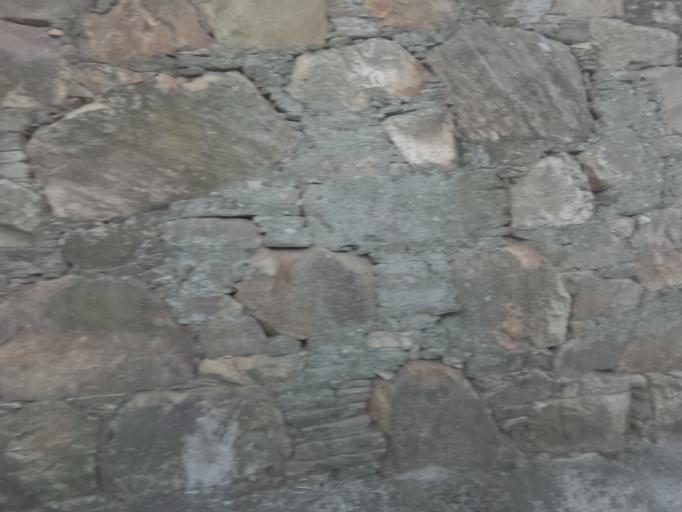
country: PT
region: Vila Real
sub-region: Peso da Regua
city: Godim
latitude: 41.1714
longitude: -7.8299
